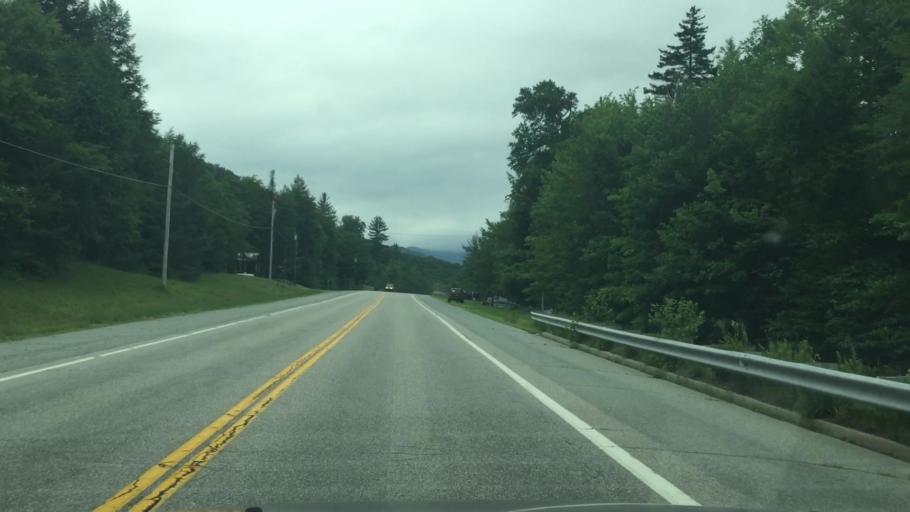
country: US
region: New Hampshire
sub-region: Carroll County
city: North Conway
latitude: 44.1084
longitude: -71.3524
